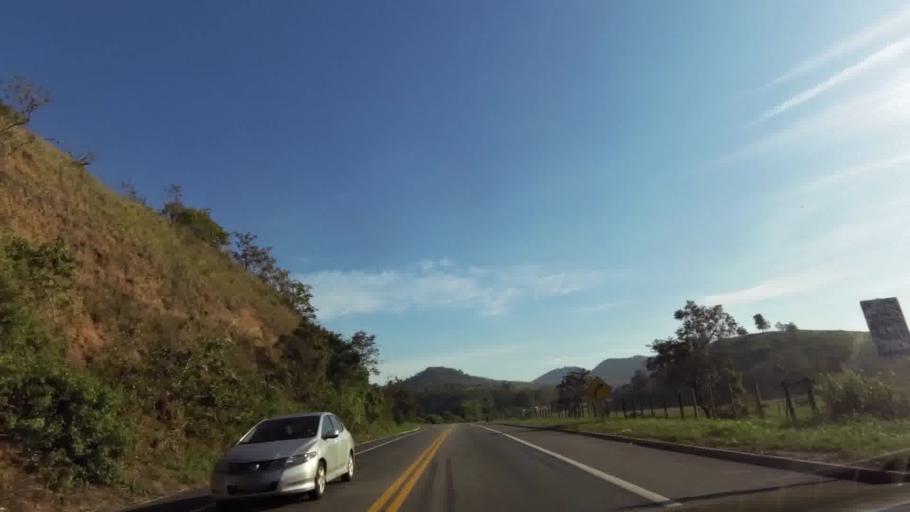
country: BR
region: Espirito Santo
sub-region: Viana
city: Viana
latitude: -20.4172
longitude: -40.4598
